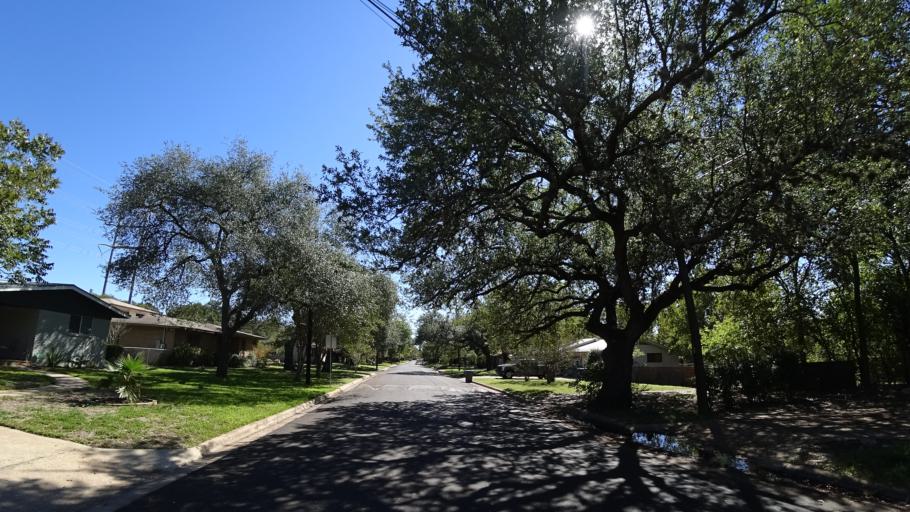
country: US
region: Texas
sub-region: Travis County
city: Rollingwood
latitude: 30.2265
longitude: -97.7947
